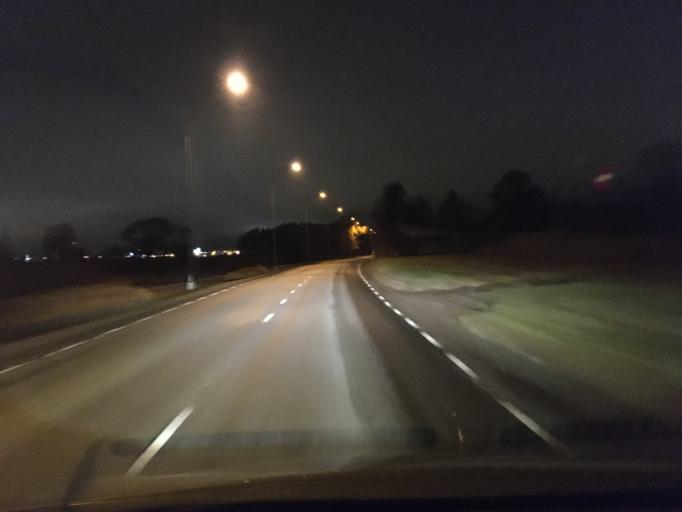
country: EE
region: Tartu
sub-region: Tartu linn
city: Tartu
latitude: 58.3632
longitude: 26.7590
